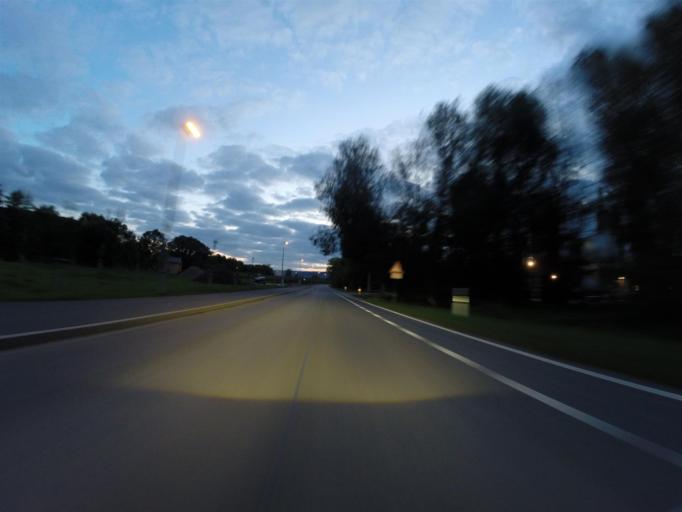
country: DE
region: Thuringia
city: Neuengonna
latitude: 50.9563
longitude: 11.6324
